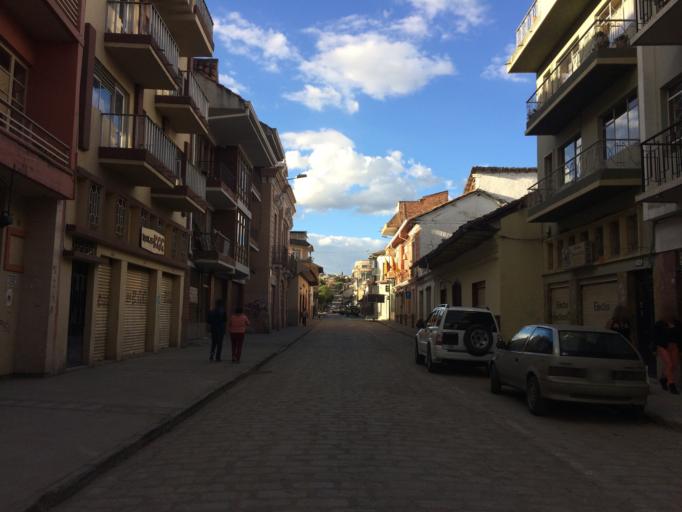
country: EC
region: Azuay
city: Cuenca
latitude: -2.8942
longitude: -79.0053
